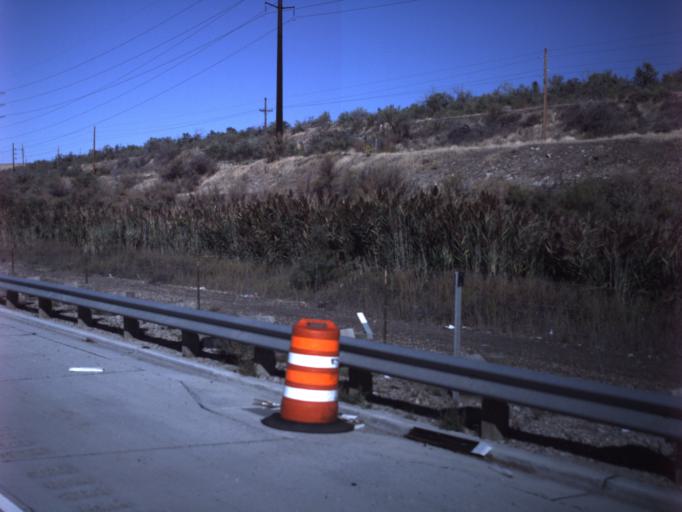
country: US
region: Utah
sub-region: Salt Lake County
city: Magna
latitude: 40.7182
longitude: -112.1083
